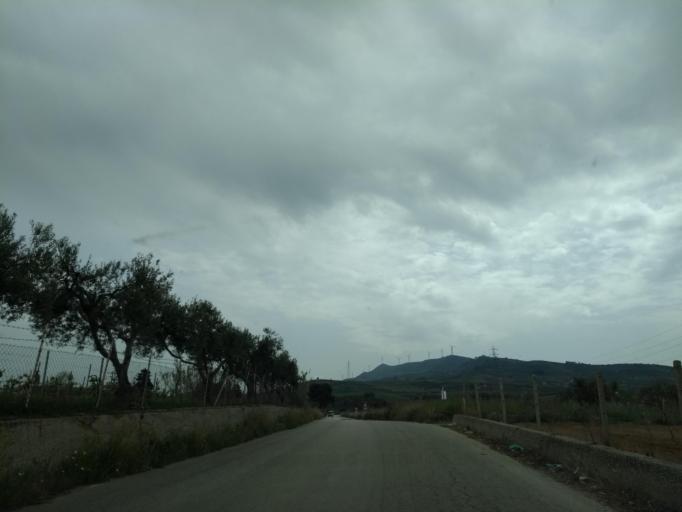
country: IT
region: Sicily
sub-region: Palermo
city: Partinico
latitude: 37.9928
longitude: 13.0663
